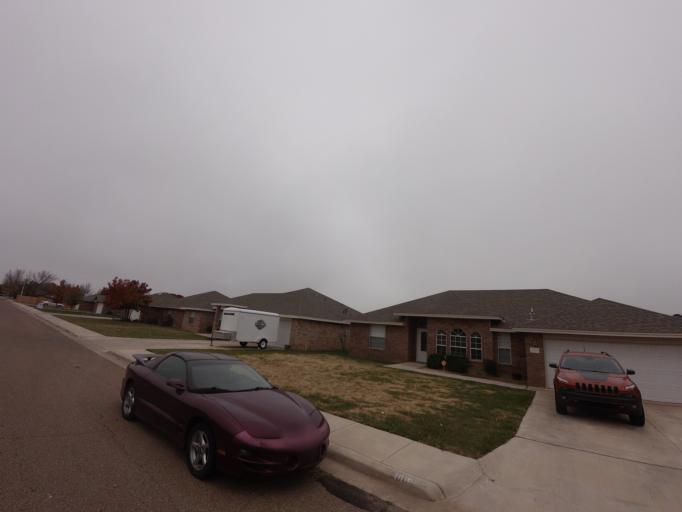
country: US
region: New Mexico
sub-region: Curry County
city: Clovis
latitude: 34.4293
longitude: -103.1838
